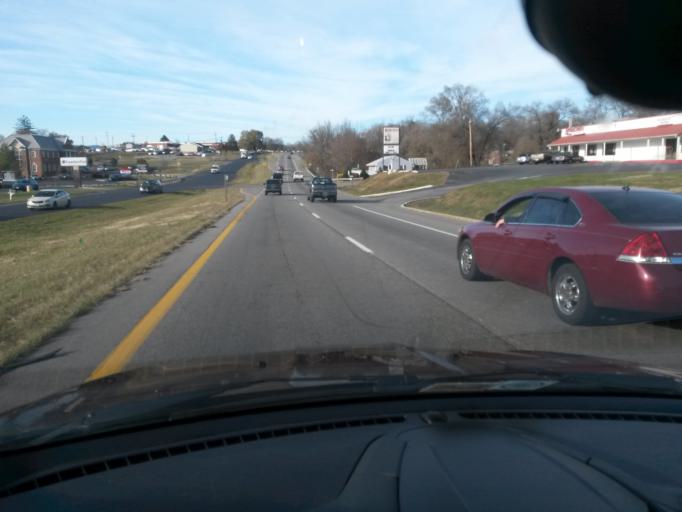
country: US
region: Virginia
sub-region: Botetourt County
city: Daleville
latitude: 37.4013
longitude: -79.9117
